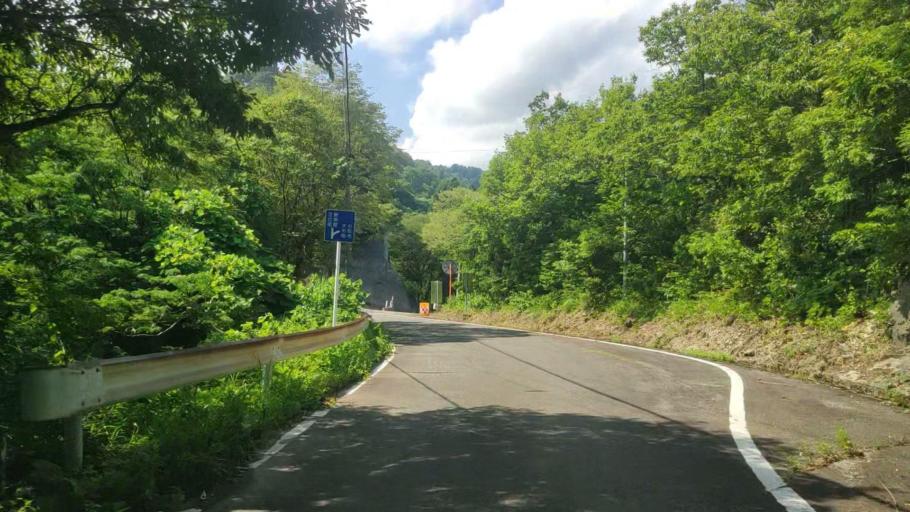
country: JP
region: Fukui
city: Katsuyama
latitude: 36.2376
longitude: 136.5289
